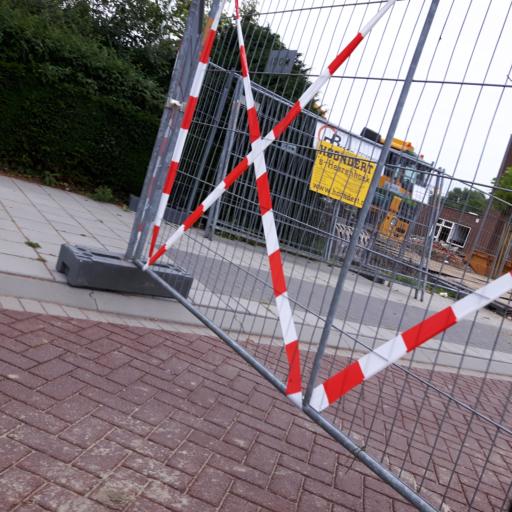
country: NL
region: Zeeland
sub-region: Gemeente Goes
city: Goes
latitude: 51.4984
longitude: 3.9033
